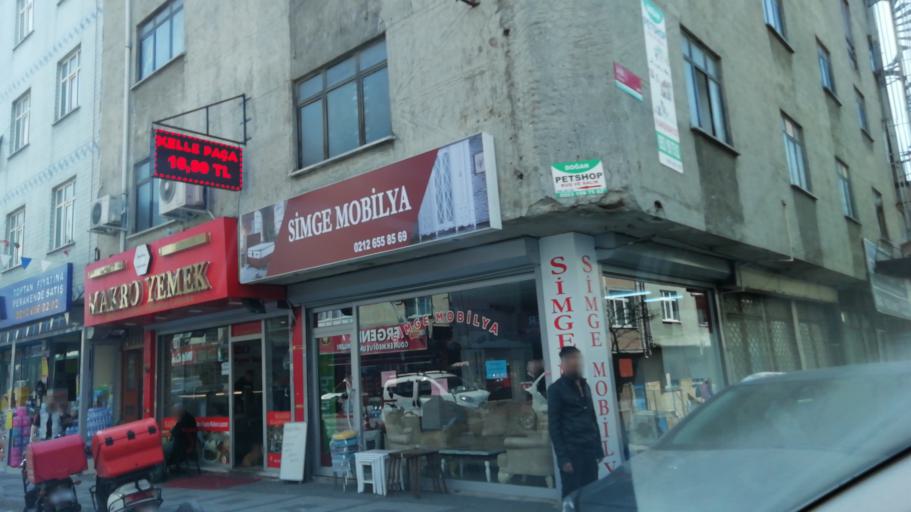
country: TR
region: Istanbul
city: Mahmutbey
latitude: 41.0337
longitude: 28.8201
